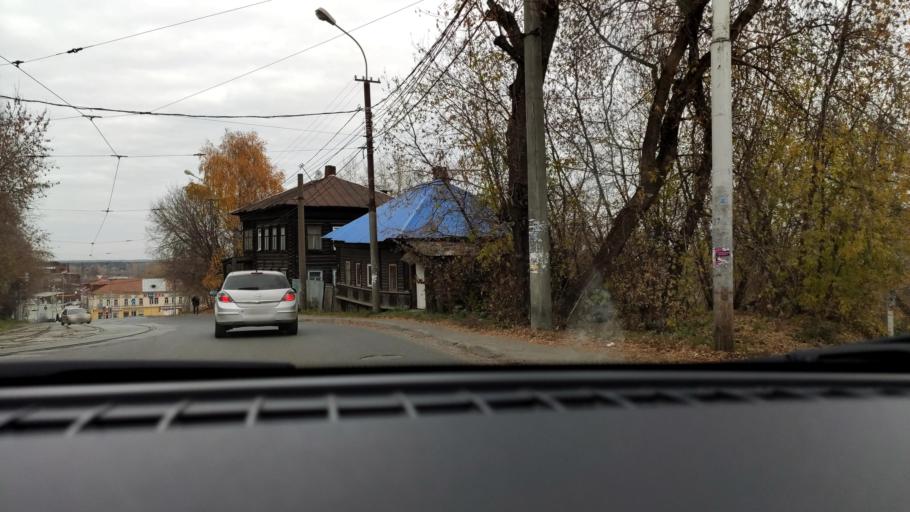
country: RU
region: Perm
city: Perm
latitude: 58.0340
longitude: 56.3129
